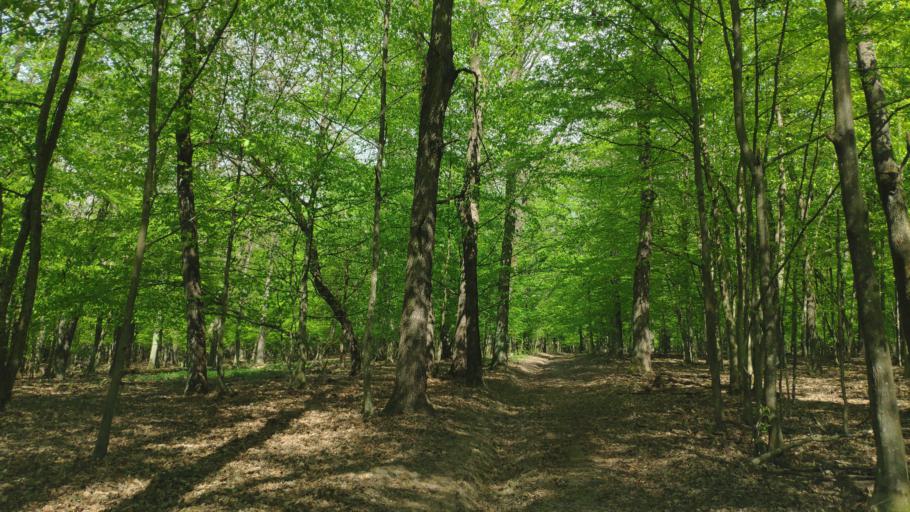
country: SK
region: Kosicky
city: Moldava nad Bodvou
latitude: 48.5515
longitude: 20.9406
